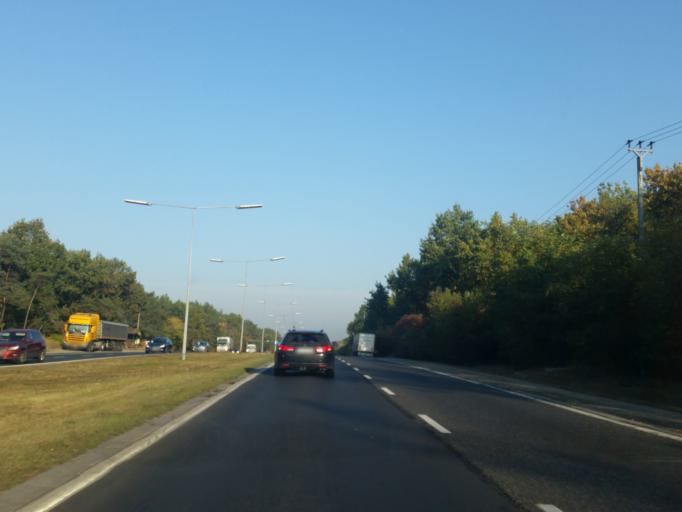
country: PL
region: Masovian Voivodeship
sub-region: Warszawa
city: Bielany
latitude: 52.3187
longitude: 20.9163
